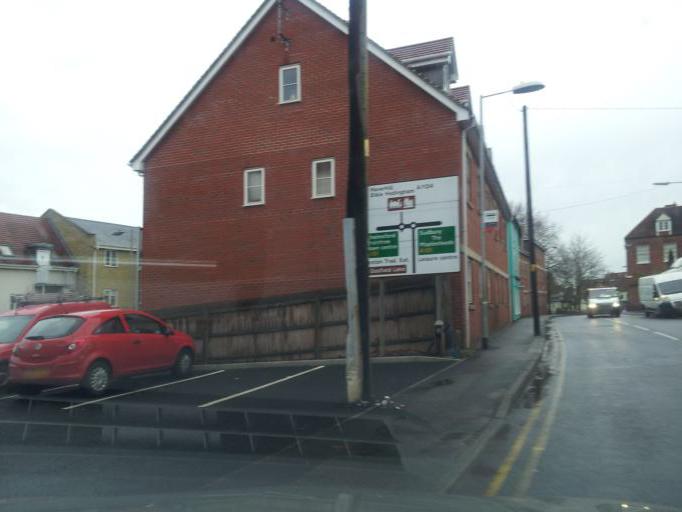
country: GB
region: England
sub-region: Essex
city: Sible Hedingham
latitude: 51.9449
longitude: 0.6419
